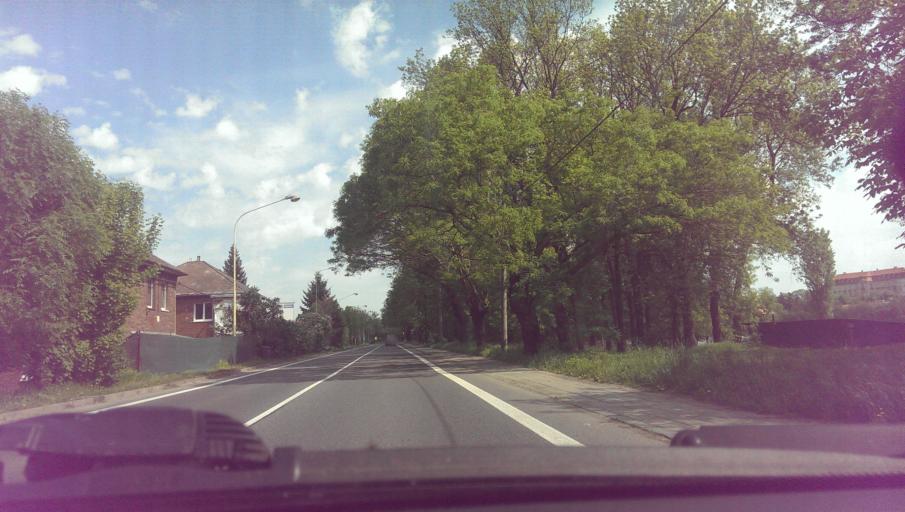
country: CZ
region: Zlin
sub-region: Okres Zlin
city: Napajedla
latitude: 49.1663
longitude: 17.5055
